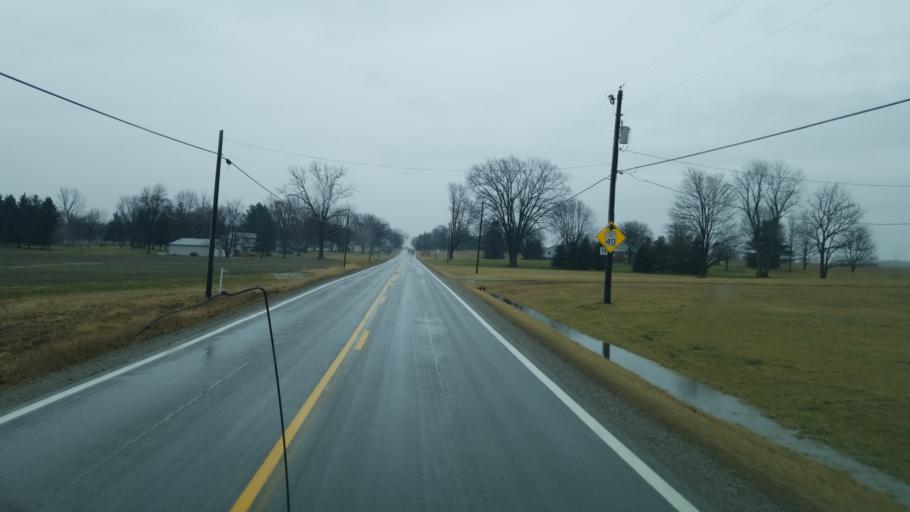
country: US
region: Ohio
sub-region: Crawford County
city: Bucyrus
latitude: 40.8677
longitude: -82.8840
